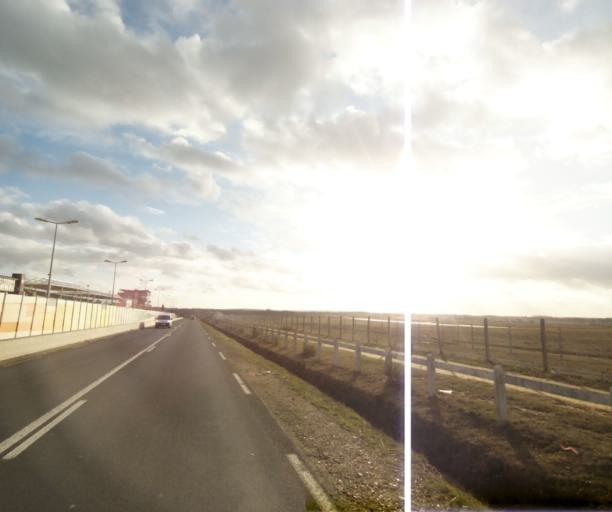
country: FR
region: Pays de la Loire
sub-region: Departement de la Sarthe
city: Arnage
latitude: 47.9550
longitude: 0.2068
